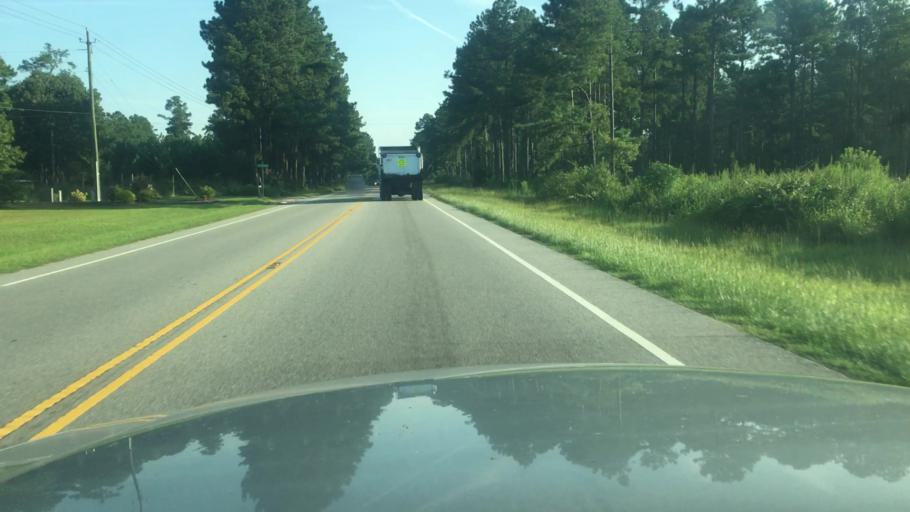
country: US
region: North Carolina
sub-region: Harnett County
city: Walkertown
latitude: 35.1951
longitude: -78.8495
